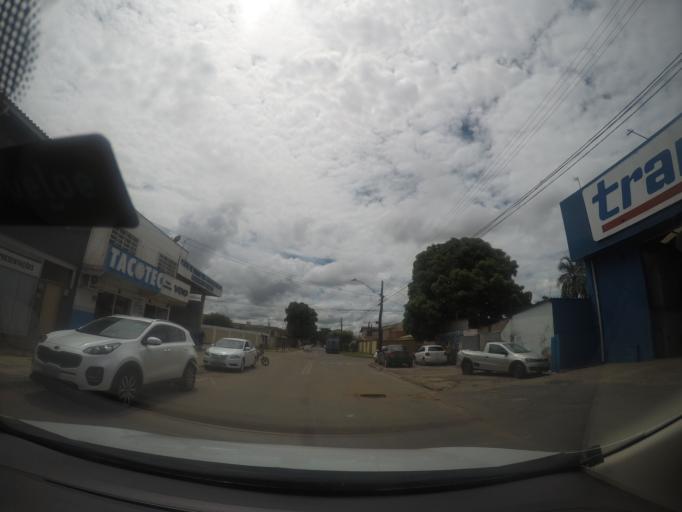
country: BR
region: Goias
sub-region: Goiania
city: Goiania
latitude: -16.6629
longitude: -49.3061
